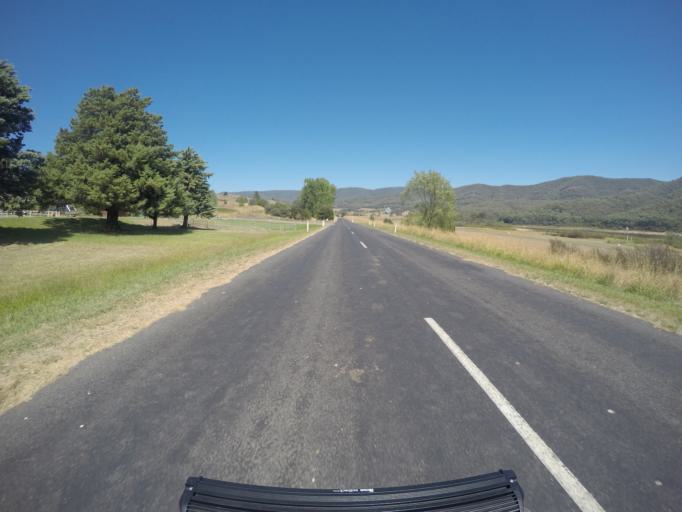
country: AU
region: New South Wales
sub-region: Tumut Shire
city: Tumut
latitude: -35.5831
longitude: 148.2934
